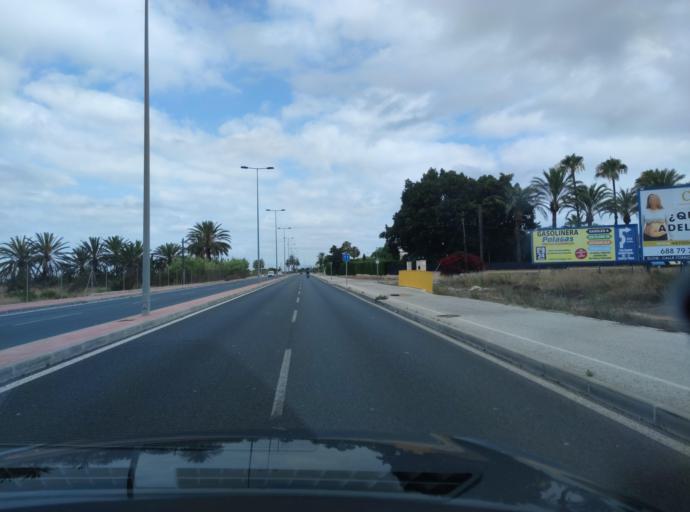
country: ES
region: Valencia
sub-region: Provincia de Alicante
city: Santa Pola
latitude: 38.2030
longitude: -0.5752
